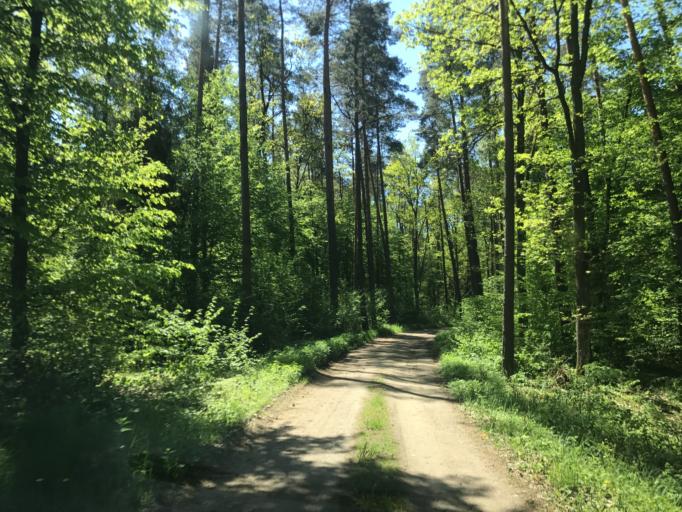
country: PL
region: Warmian-Masurian Voivodeship
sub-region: Powiat dzialdowski
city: Lidzbark
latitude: 53.2586
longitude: 19.7523
